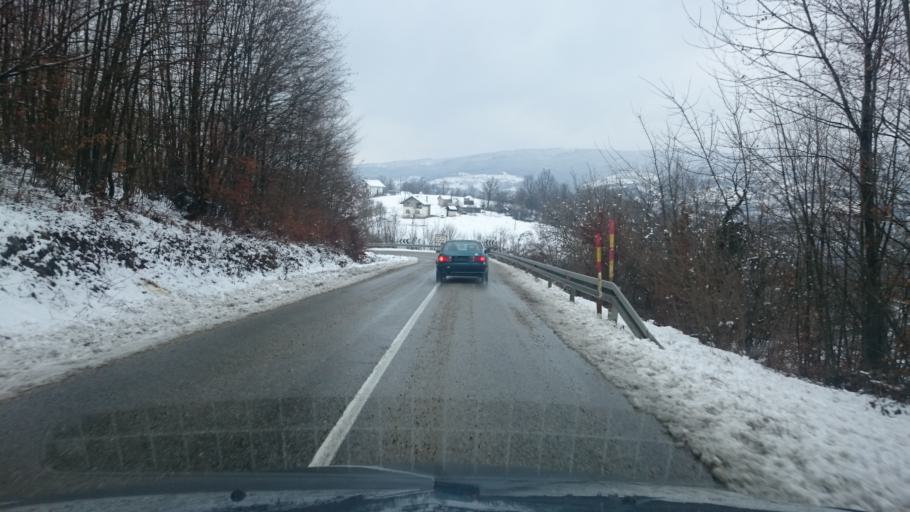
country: BA
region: Republika Srpska
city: Starcevica
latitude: 44.6806
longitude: 17.2116
